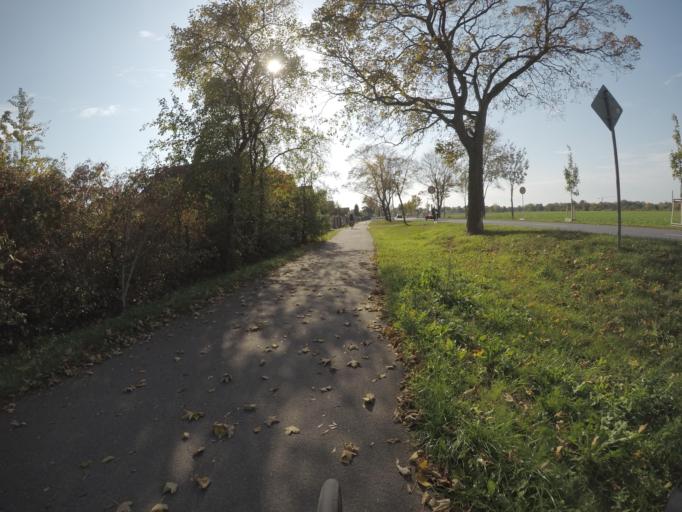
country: DE
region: Brandenburg
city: Velten
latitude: 52.6914
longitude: 13.1975
